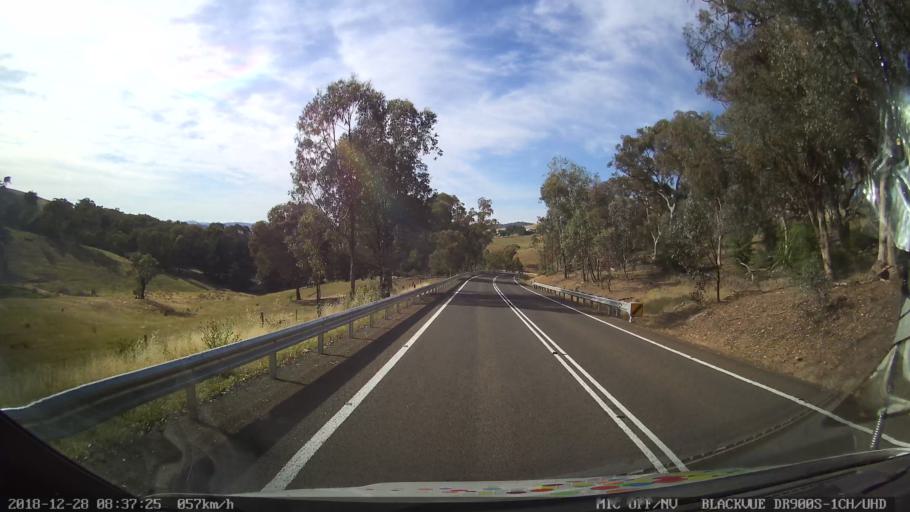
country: AU
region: New South Wales
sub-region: Blayney
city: Blayney
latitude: -33.9951
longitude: 149.3131
